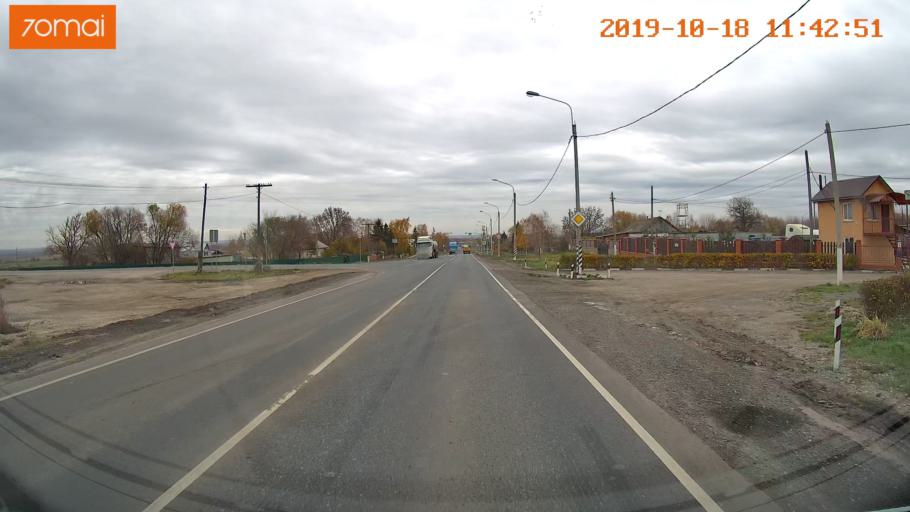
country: RU
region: Rjazan
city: Oktyabr'skiy
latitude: 54.1922
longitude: 38.9354
